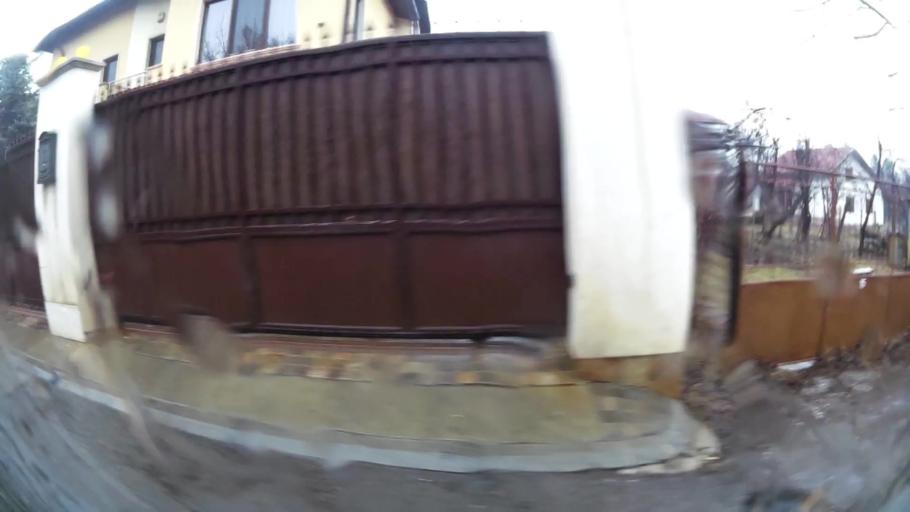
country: BG
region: Sofia-Capital
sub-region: Stolichna Obshtina
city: Sofia
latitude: 42.6261
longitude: 23.3634
